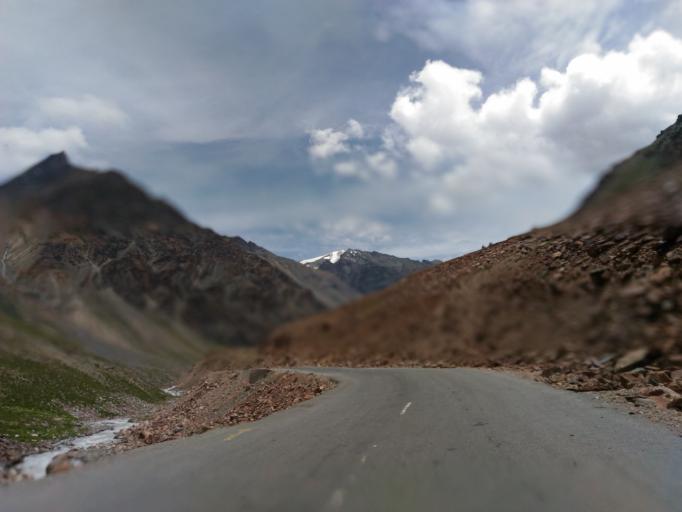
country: IN
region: Himachal Pradesh
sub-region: Lahul and Spiti
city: Kyelang
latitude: 32.7917
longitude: 77.3148
